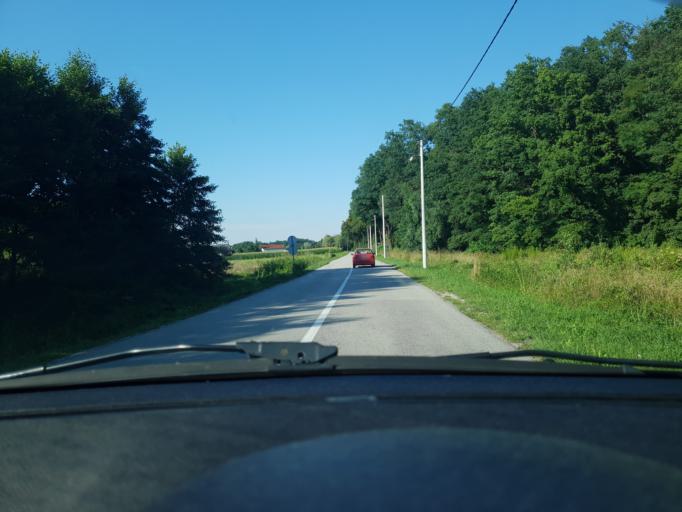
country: HR
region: Zagrebacka
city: Jakovlje
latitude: 45.9564
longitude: 15.8523
